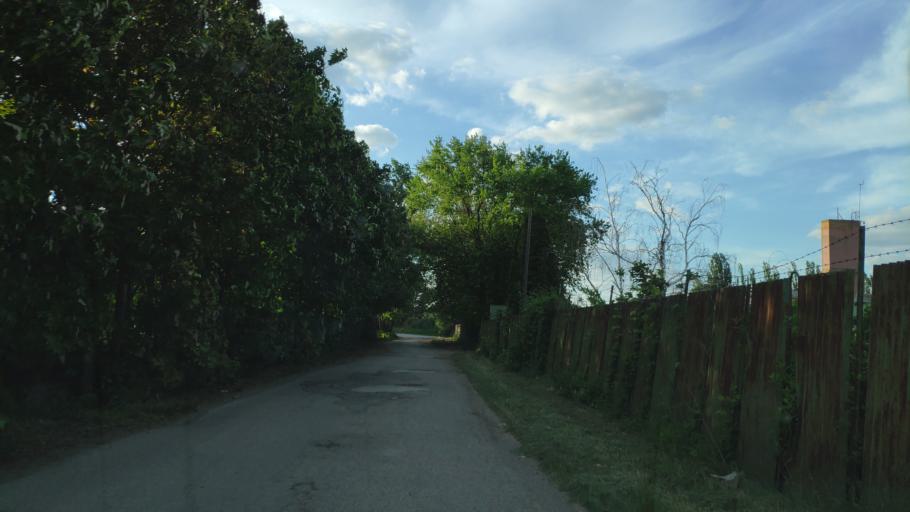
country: SK
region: Kosicky
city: Kosice
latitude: 48.6570
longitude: 21.3158
